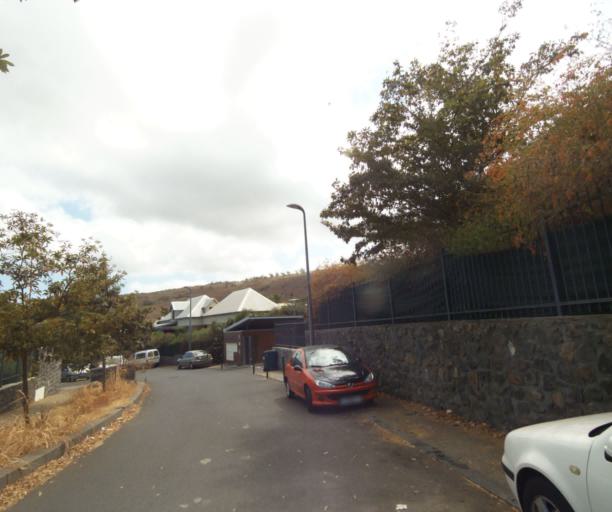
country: RE
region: Reunion
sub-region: Reunion
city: Trois-Bassins
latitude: -21.0858
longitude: 55.2385
